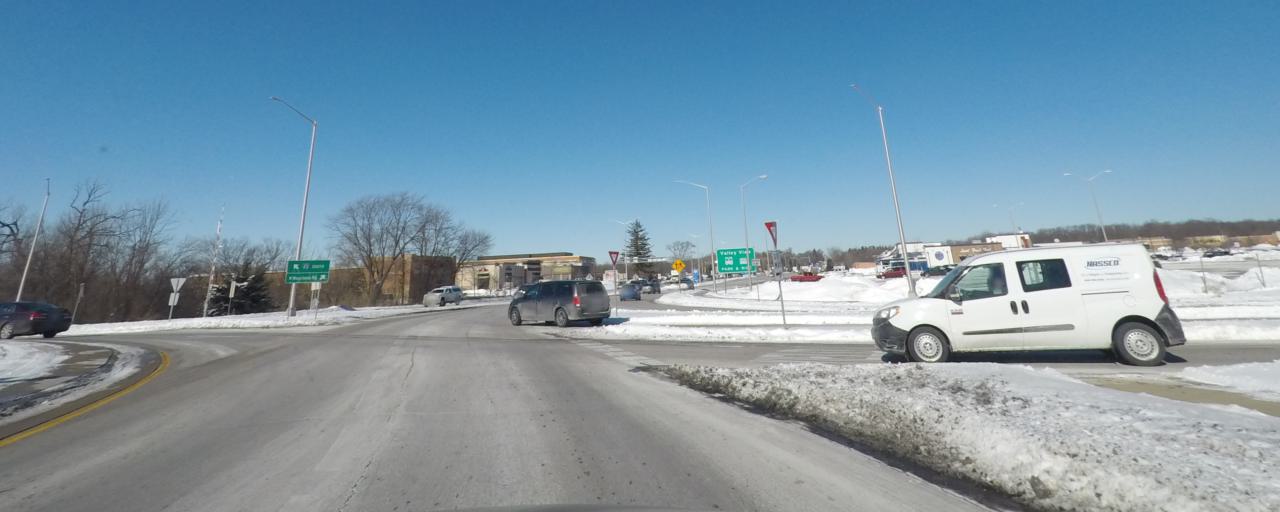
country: US
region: Wisconsin
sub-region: Waukesha County
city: New Berlin
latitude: 42.9535
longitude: -88.1085
